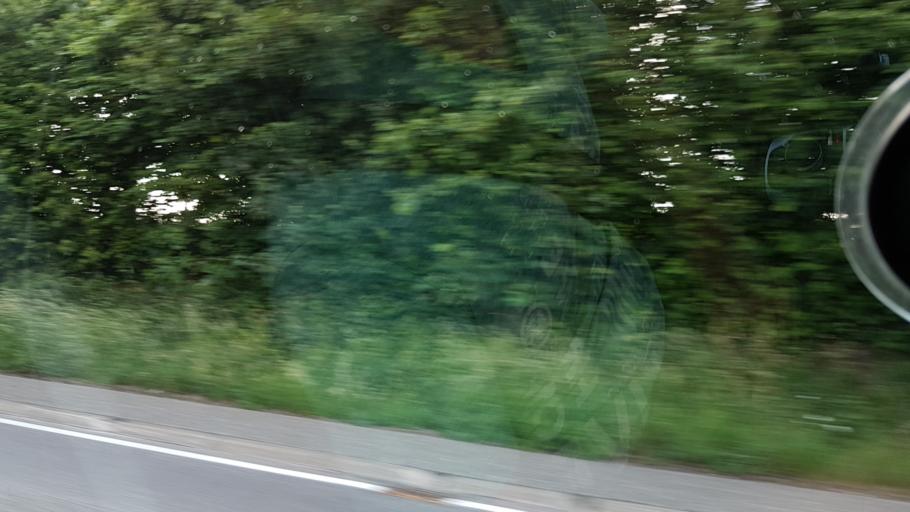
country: DE
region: Rheinland-Pfalz
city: Eckersweiler
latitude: 49.5585
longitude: 7.2716
